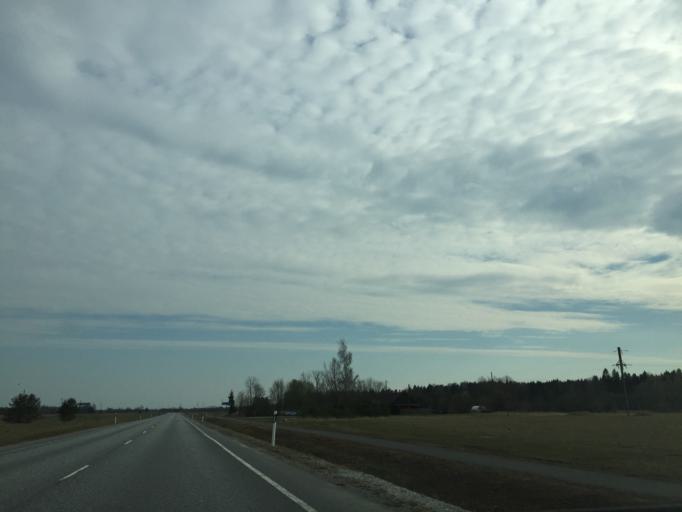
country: EE
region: Ida-Virumaa
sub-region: Johvi vald
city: Johvi
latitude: 59.2899
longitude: 27.4963
